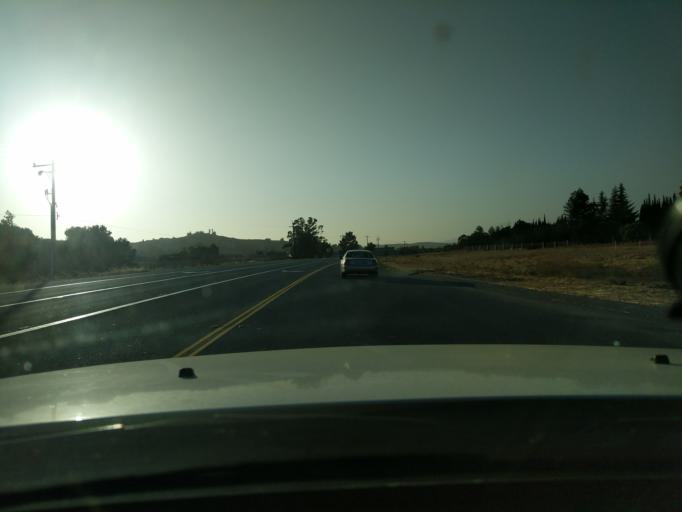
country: US
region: California
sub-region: San Benito County
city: Ridgemark
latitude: 36.8164
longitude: -121.3639
